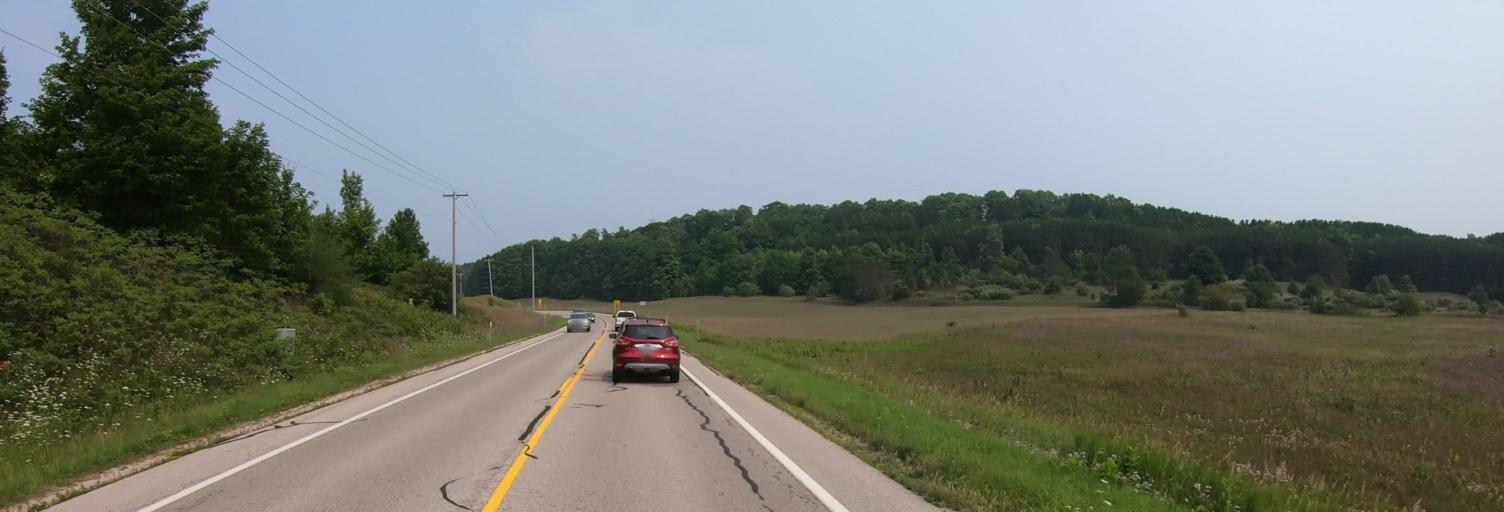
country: US
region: Michigan
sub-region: Leelanau County
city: Leland
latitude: 45.0946
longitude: -85.6613
